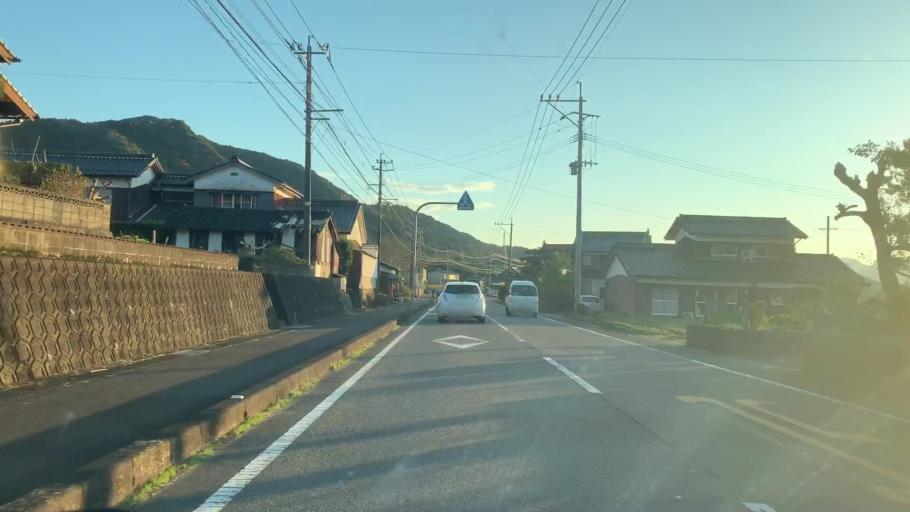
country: JP
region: Saga Prefecture
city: Imaricho-ko
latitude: 33.2849
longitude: 129.9698
